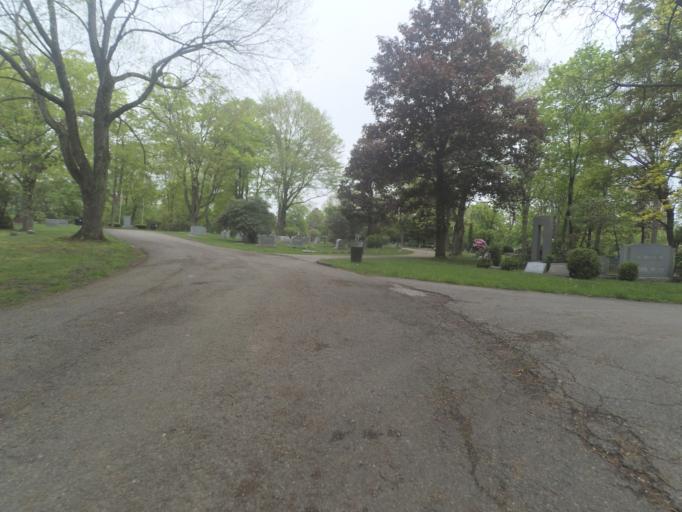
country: US
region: Ohio
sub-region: Portage County
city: Kent
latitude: 41.1674
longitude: -81.3512
